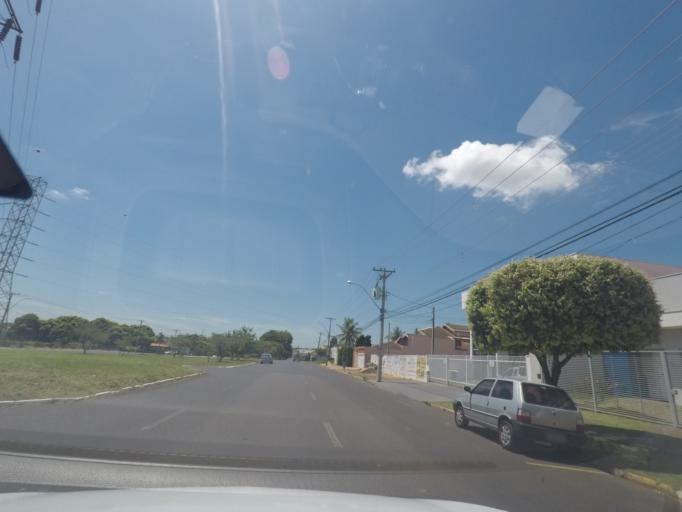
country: BR
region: Sao Paulo
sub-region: Matao
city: Matao
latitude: -21.6162
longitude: -48.3654
